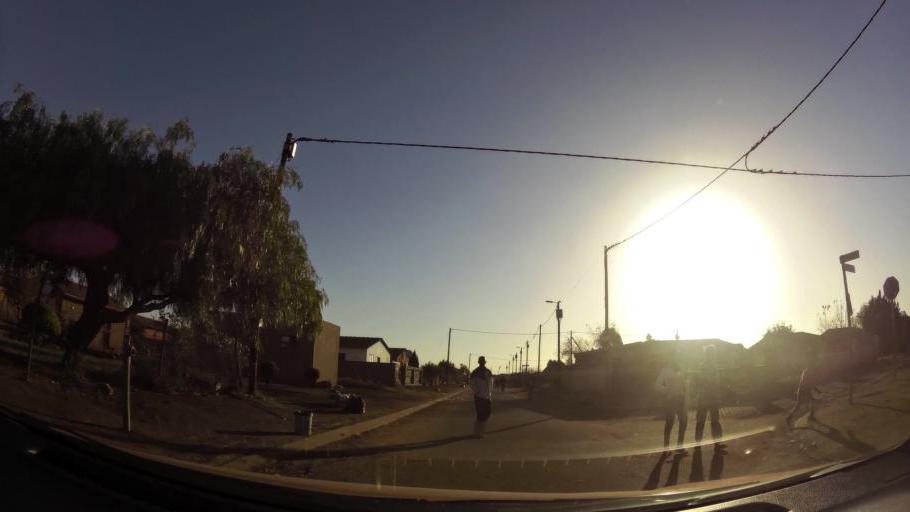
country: ZA
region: Gauteng
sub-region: City of Tshwane Metropolitan Municipality
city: Mabopane
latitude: -25.6007
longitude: 28.1033
